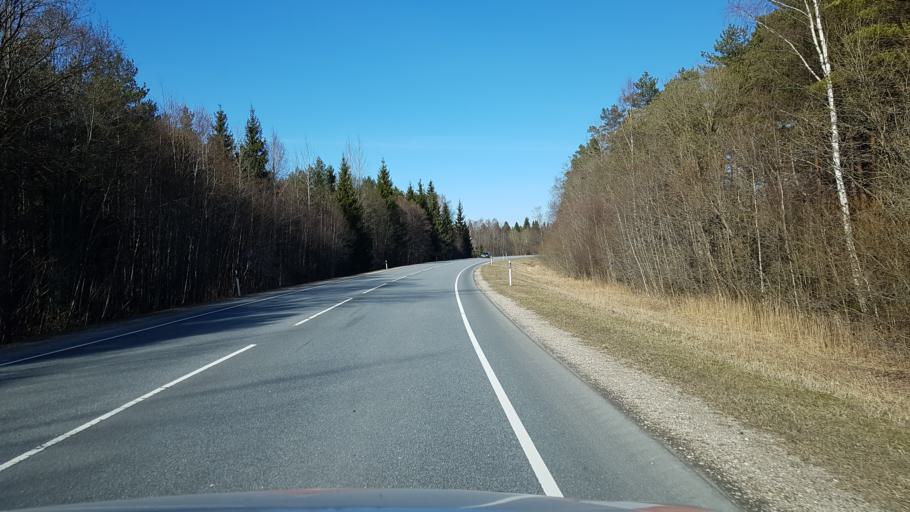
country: EE
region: Harju
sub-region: Nissi vald
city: Turba
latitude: 59.0661
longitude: 24.1946
